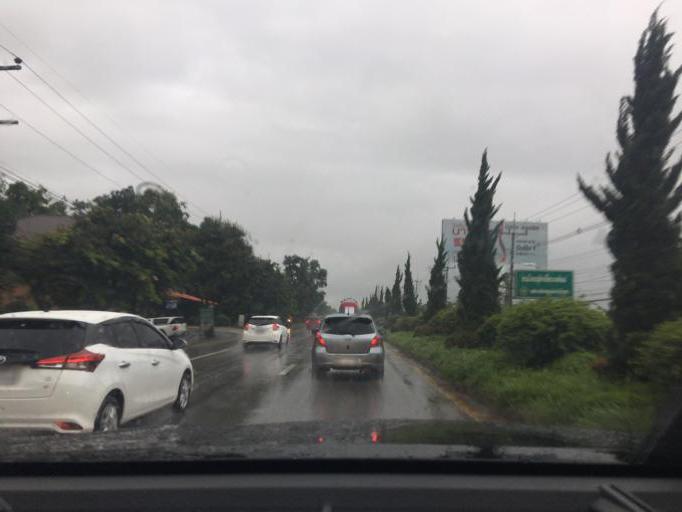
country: TH
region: Chiang Rai
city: Chiang Rai
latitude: 20.0150
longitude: 99.8695
